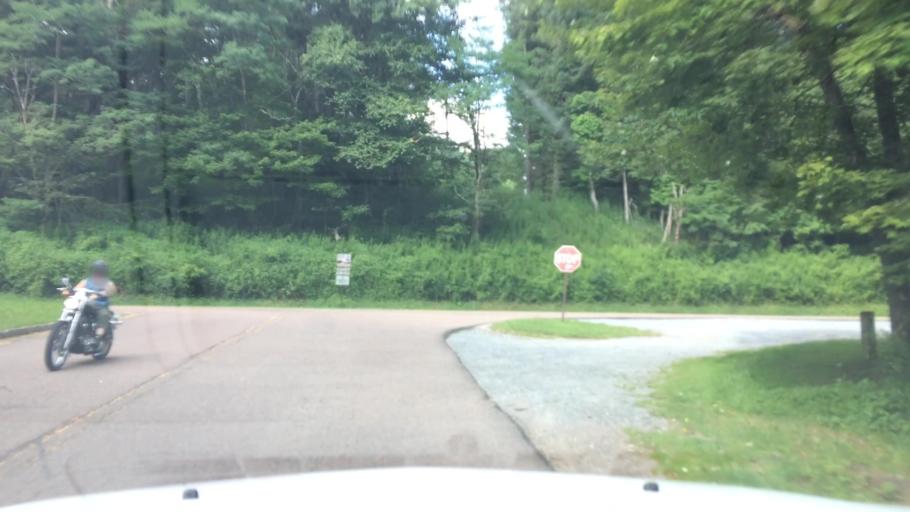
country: US
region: North Carolina
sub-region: Watauga County
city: Blowing Rock
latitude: 36.1483
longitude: -81.6640
